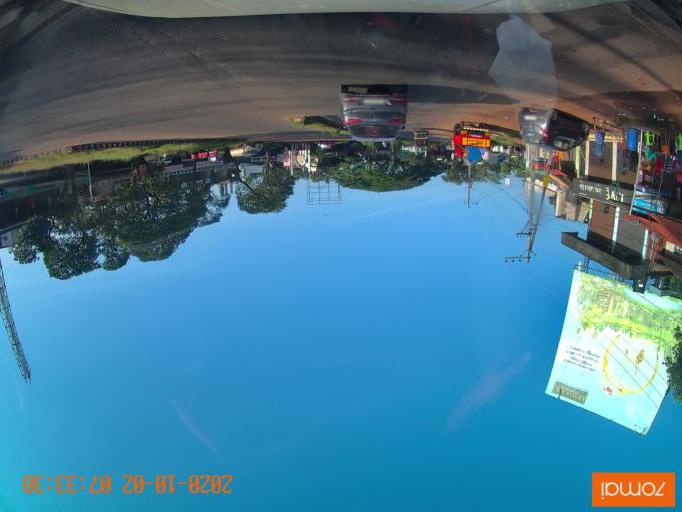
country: IN
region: Kerala
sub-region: Malappuram
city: Pariyapuram
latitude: 11.0604
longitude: 75.9358
